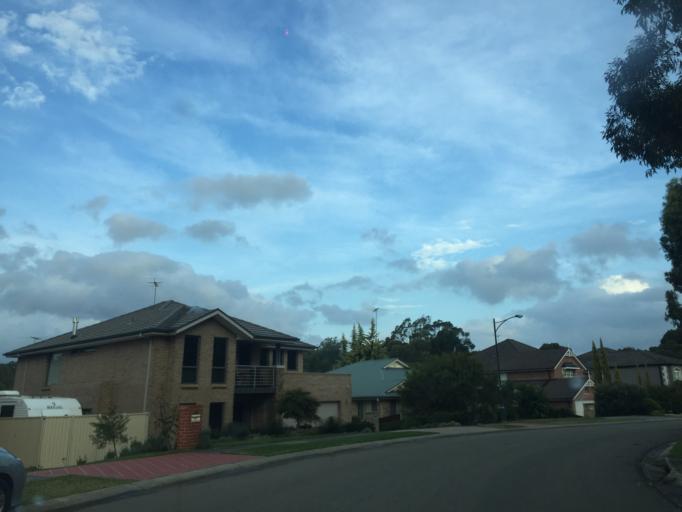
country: AU
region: New South Wales
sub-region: The Hills Shire
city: Glenhaven
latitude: -33.6996
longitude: 150.9751
